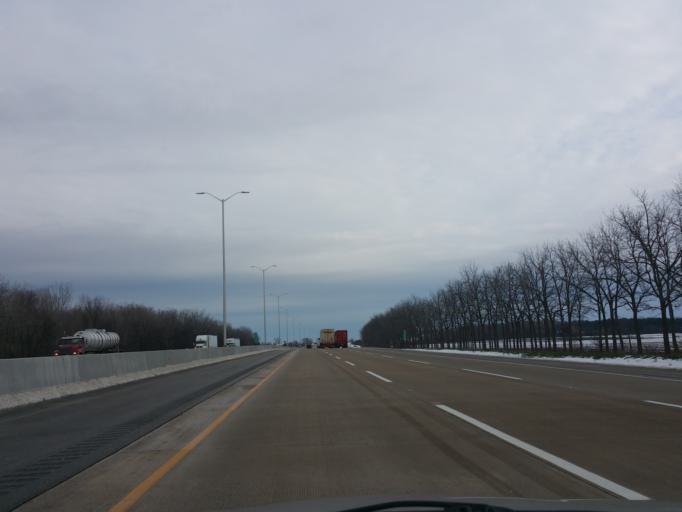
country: US
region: Illinois
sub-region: McHenry County
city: Marengo
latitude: 42.2001
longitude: -88.6838
